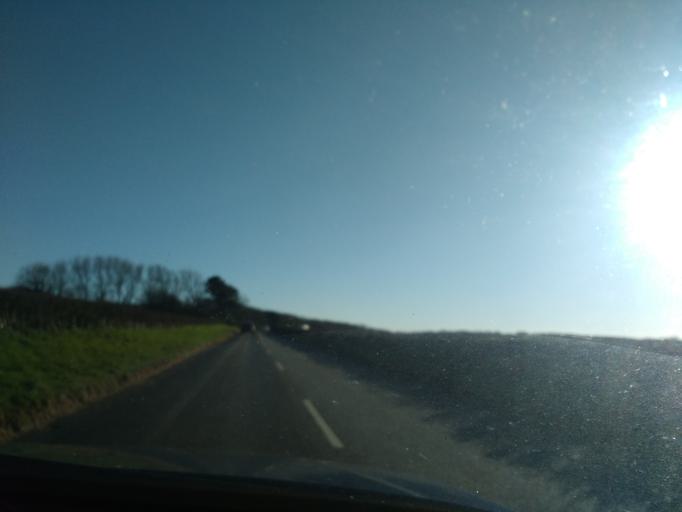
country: GB
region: England
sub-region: Isle of Wight
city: Newchurch
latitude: 50.6997
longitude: -1.2417
